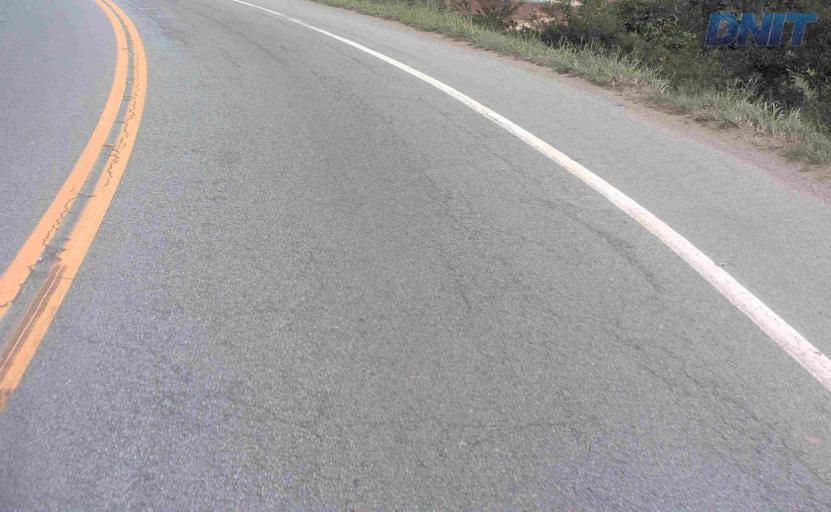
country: BR
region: Minas Gerais
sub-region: Caete
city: Caete
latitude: -19.7576
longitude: -43.6358
